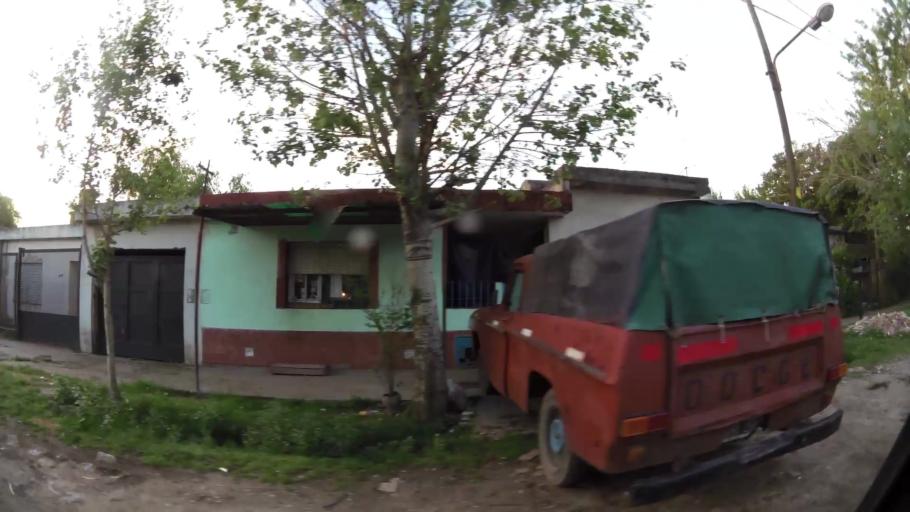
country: AR
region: Buenos Aires
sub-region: Partido de Quilmes
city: Quilmes
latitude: -34.7886
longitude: -58.2207
